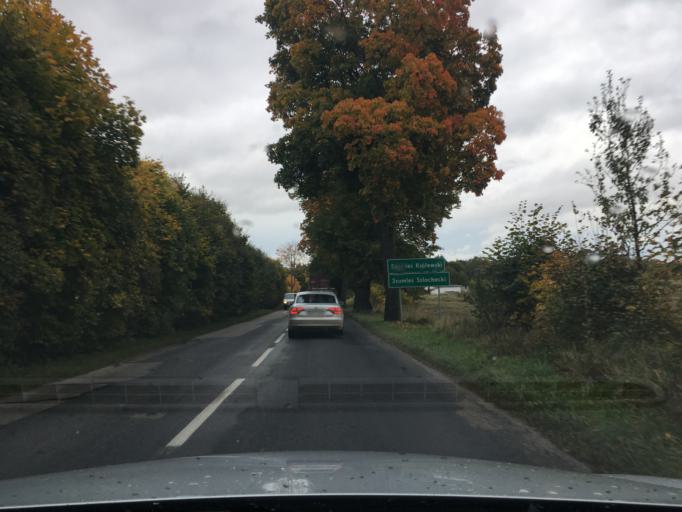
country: PL
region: Pomeranian Voivodeship
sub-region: Powiat koscierski
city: Liniewo
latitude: 54.1398
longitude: 18.2365
